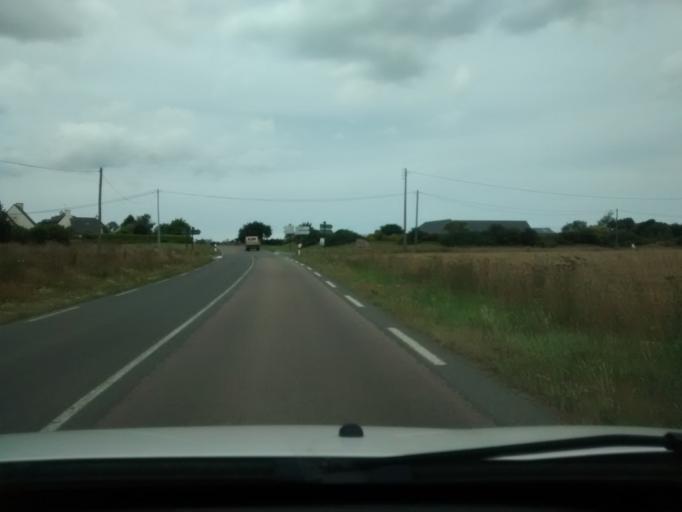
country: FR
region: Brittany
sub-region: Departement des Cotes-d'Armor
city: Trelevern
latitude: 48.7737
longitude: -3.3688
